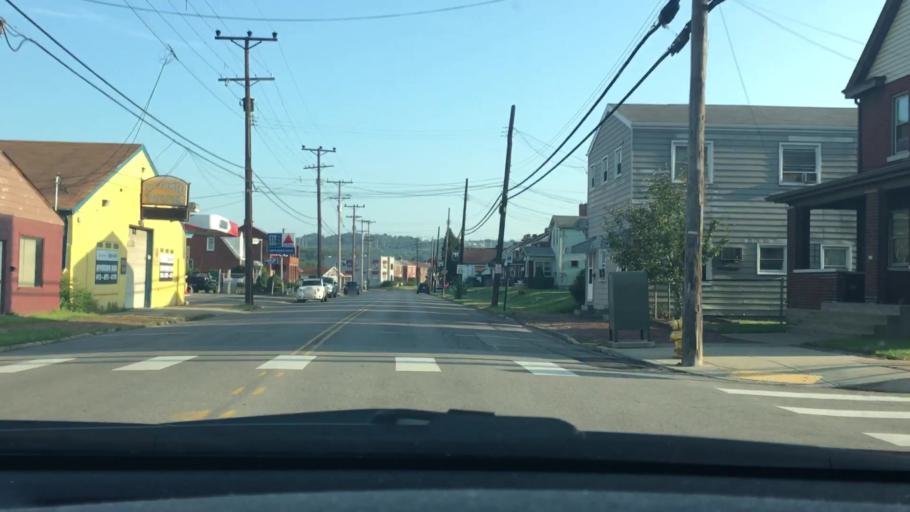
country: US
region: Pennsylvania
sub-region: Allegheny County
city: Glassport
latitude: 40.3291
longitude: -79.8925
